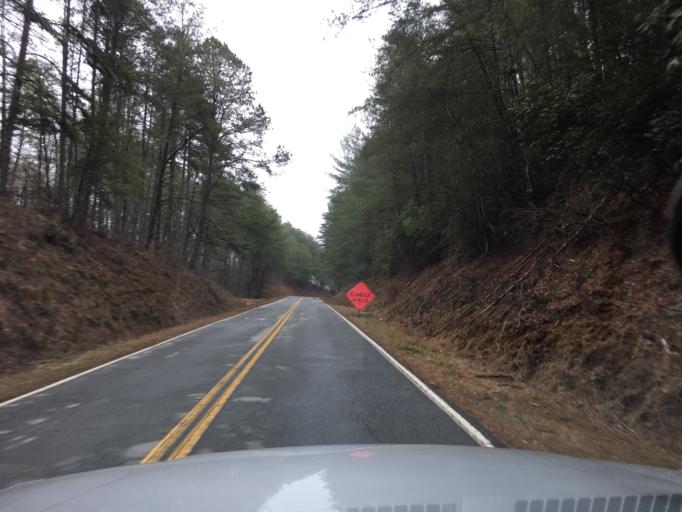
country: US
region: South Carolina
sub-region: Oconee County
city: Walhalla
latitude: 34.7888
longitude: -83.2079
